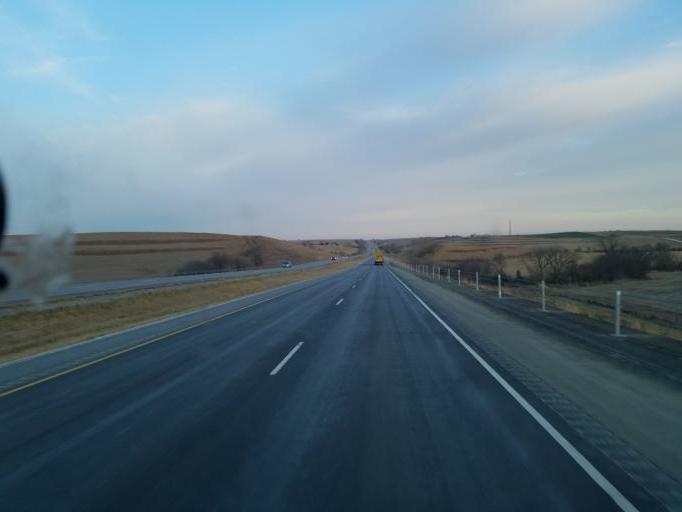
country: US
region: Iowa
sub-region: Harrison County
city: Logan
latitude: 41.4983
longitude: -95.6939
